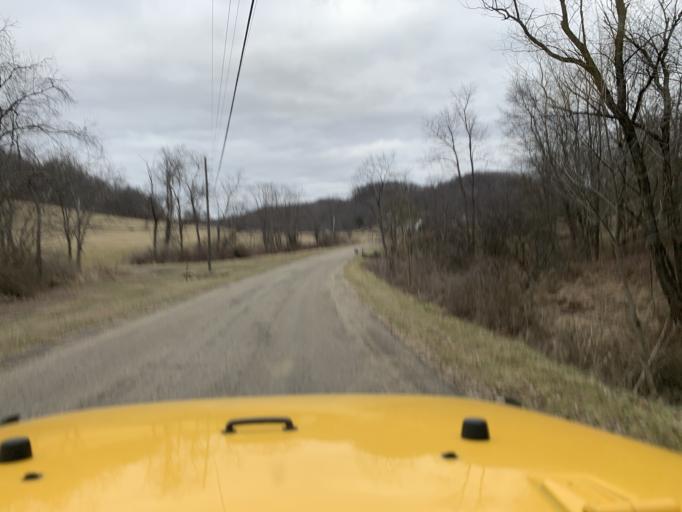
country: US
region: Ohio
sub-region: Tuscarawas County
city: Newcomerstown
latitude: 40.2986
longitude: -81.5553
